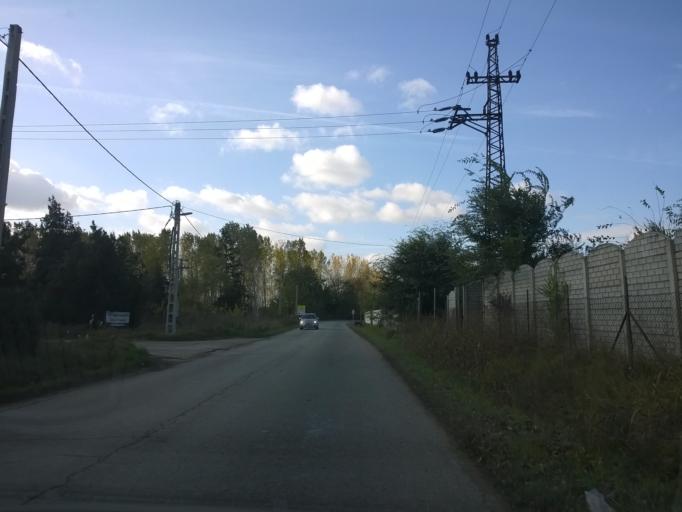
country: HU
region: Pest
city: Rackeve
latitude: 47.1520
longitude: 18.9207
